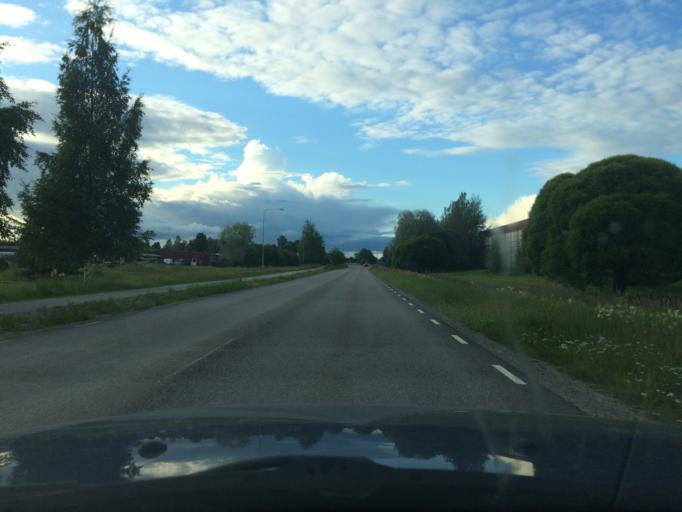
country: SE
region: Norrbotten
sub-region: Pitea Kommun
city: Bergsviken
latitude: 65.3425
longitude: 21.4062
